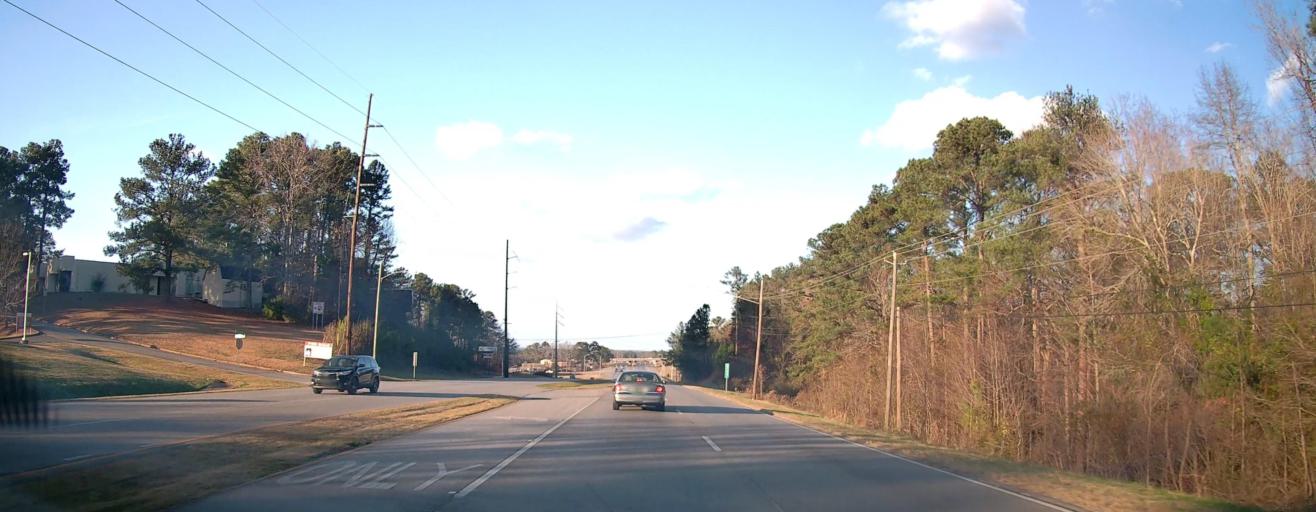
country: US
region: Alabama
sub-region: Calhoun County
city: Saks
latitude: 33.6914
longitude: -85.8231
